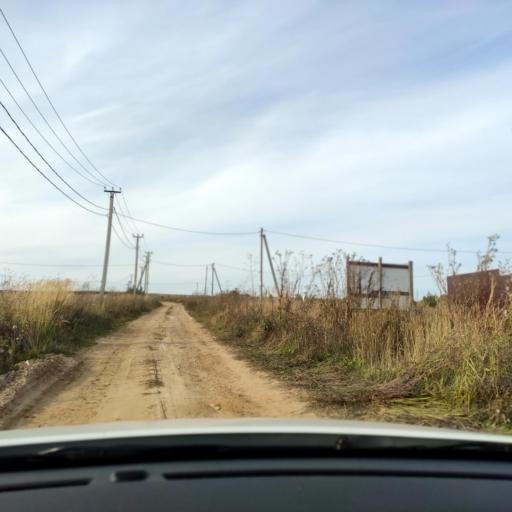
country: RU
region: Tatarstan
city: Vysokaya Gora
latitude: 55.9662
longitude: 49.2086
